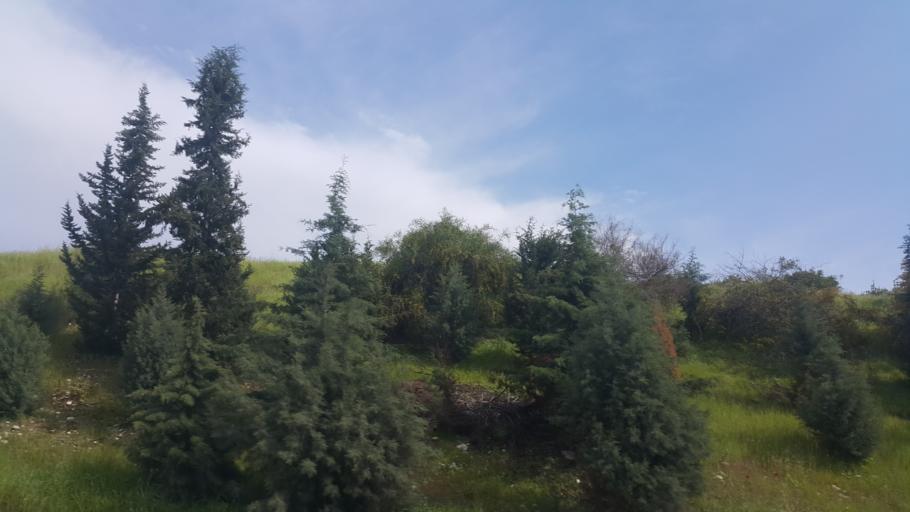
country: TR
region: Mersin
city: Mercin
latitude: 36.9060
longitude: 34.6720
